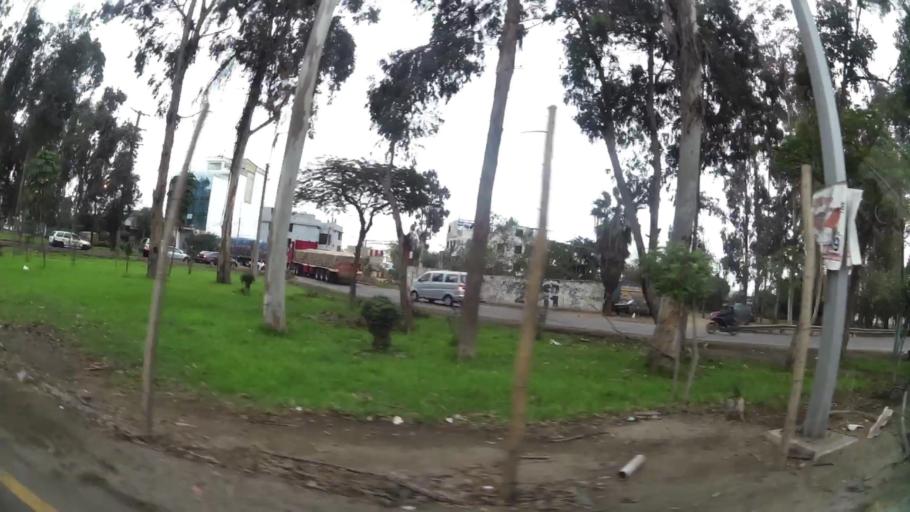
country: PE
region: Lima
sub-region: Lima
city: La Molina
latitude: -12.0655
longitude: -76.9679
